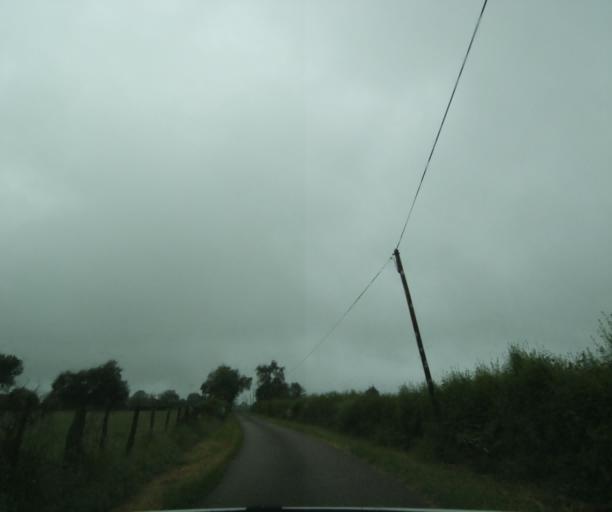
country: FR
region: Bourgogne
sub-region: Departement de Saone-et-Loire
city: Charolles
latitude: 46.4594
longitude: 4.2106
